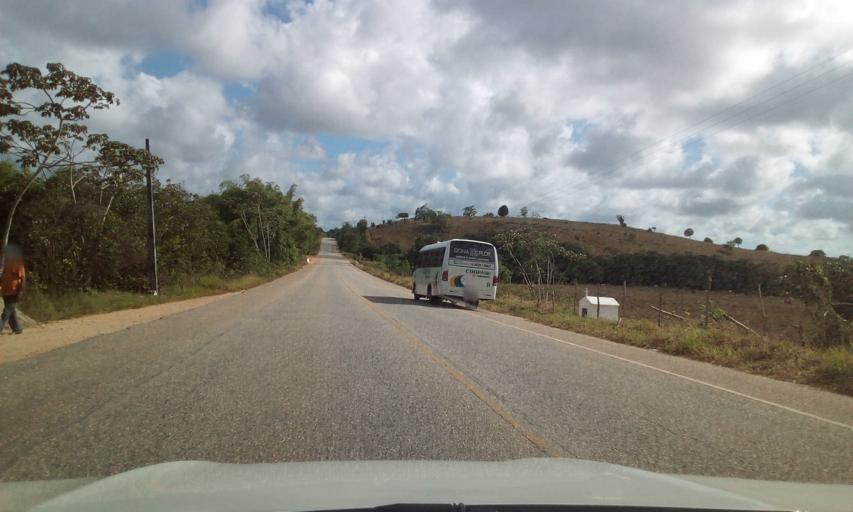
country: BR
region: Sergipe
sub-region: Indiaroba
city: Indiaroba
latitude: -11.4092
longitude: -37.4877
